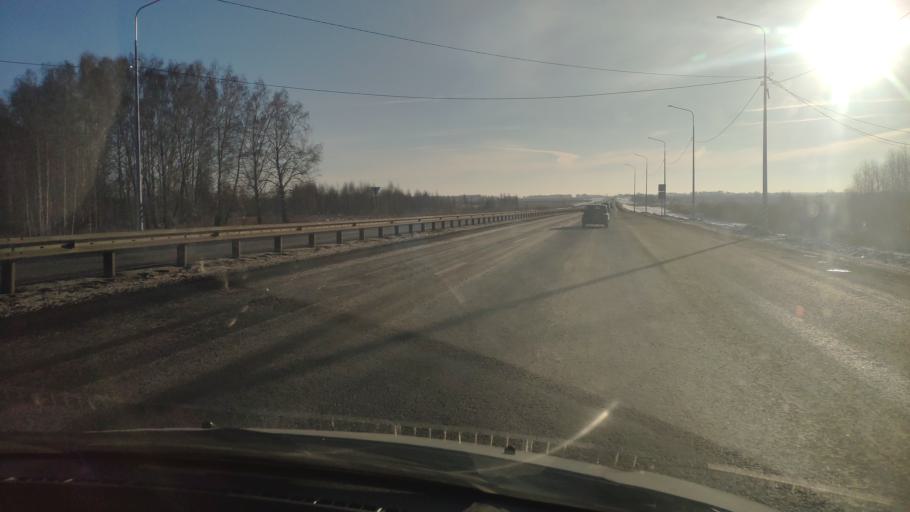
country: RU
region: Chelyabinsk
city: Tyubuk
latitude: 55.8539
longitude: 61.1673
